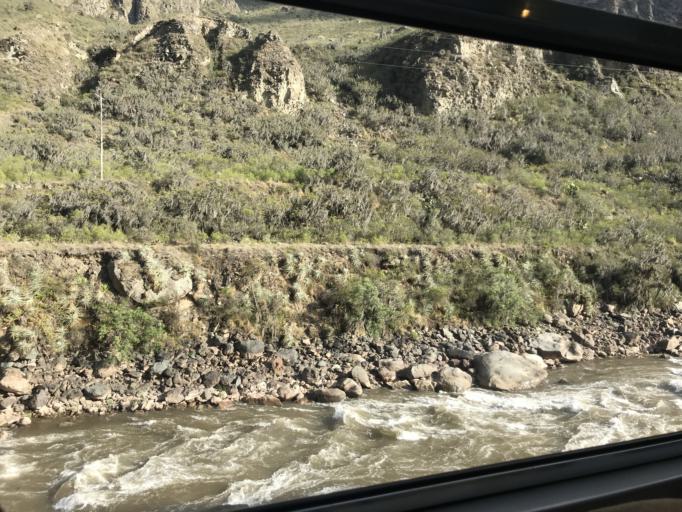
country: PE
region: Cusco
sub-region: Provincia de Urubamba
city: Ollantaytambo
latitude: -13.2252
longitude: -72.3983
